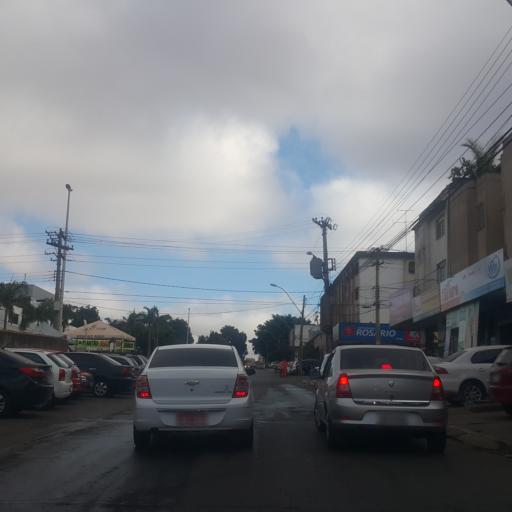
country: BR
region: Federal District
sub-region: Brasilia
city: Brasilia
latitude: -15.8234
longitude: -48.0655
